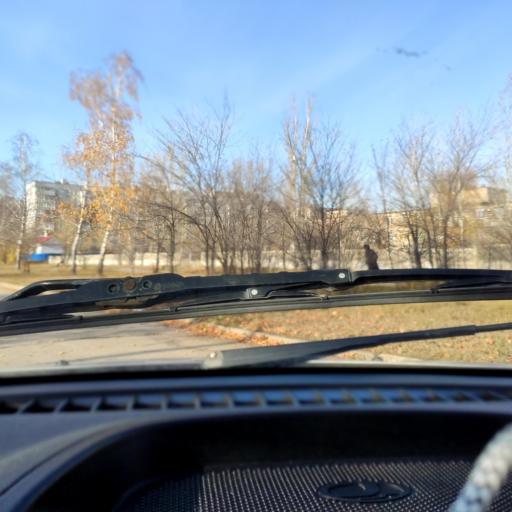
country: RU
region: Samara
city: Zhigulevsk
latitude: 53.4674
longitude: 49.5392
